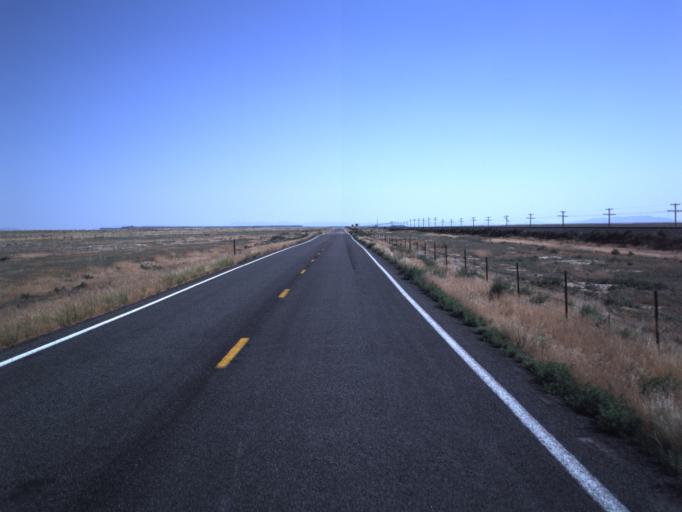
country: US
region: Utah
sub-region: Millard County
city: Delta
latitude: 39.0049
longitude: -112.7856
